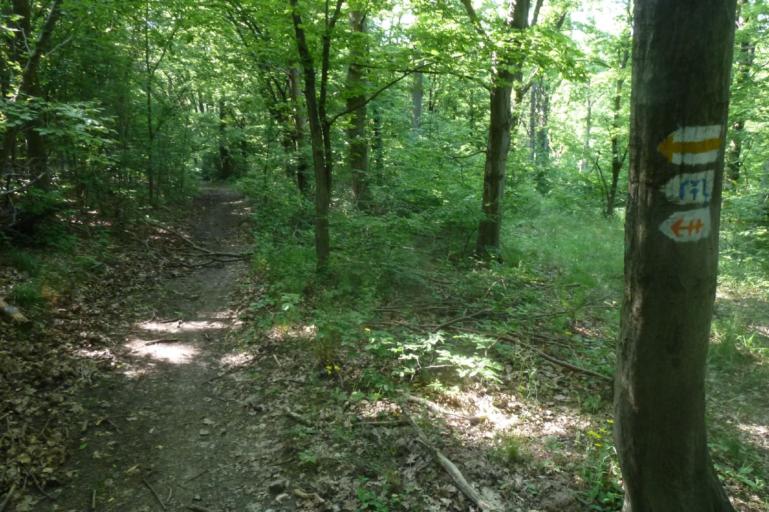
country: HU
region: Pest
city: Pilisszentkereszt
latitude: 47.7006
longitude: 18.9127
